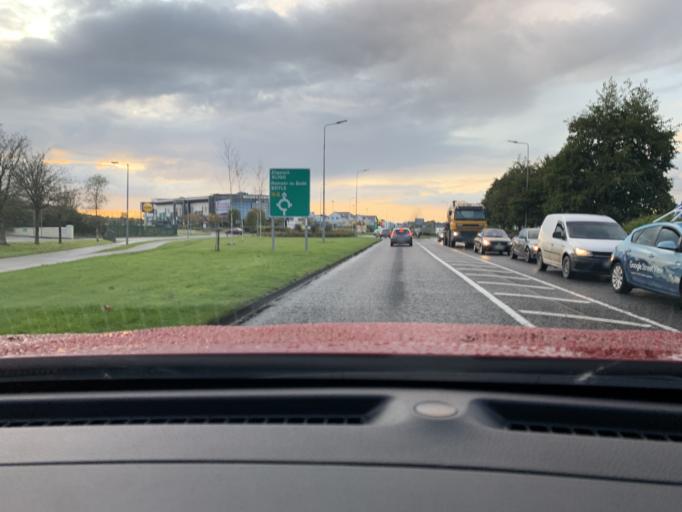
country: IE
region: Connaught
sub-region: County Leitrim
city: Carrick-on-Shannon
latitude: 53.9417
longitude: -8.1028
